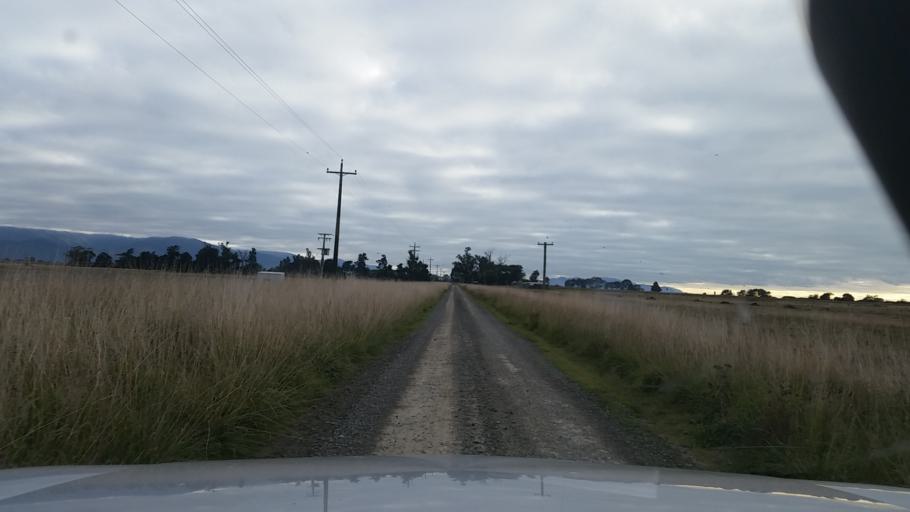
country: NZ
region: Marlborough
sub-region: Marlborough District
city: Blenheim
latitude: -41.5049
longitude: 174.0314
